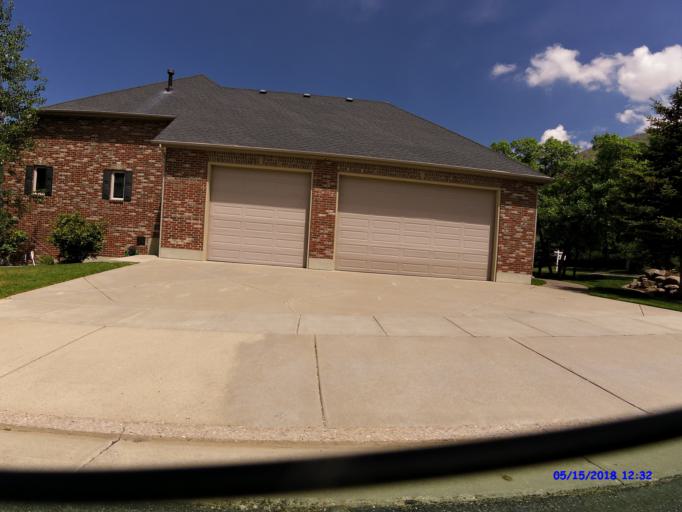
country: US
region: Utah
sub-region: Weber County
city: Uintah
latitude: 41.1753
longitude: -111.9324
